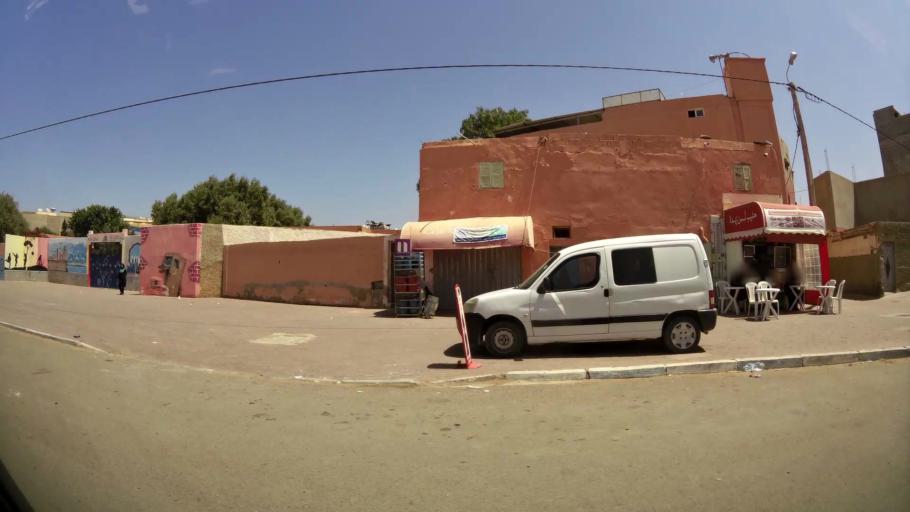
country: MA
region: Souss-Massa-Draa
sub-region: Inezgane-Ait Mellou
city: Inezgane
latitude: 30.3346
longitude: -9.4974
